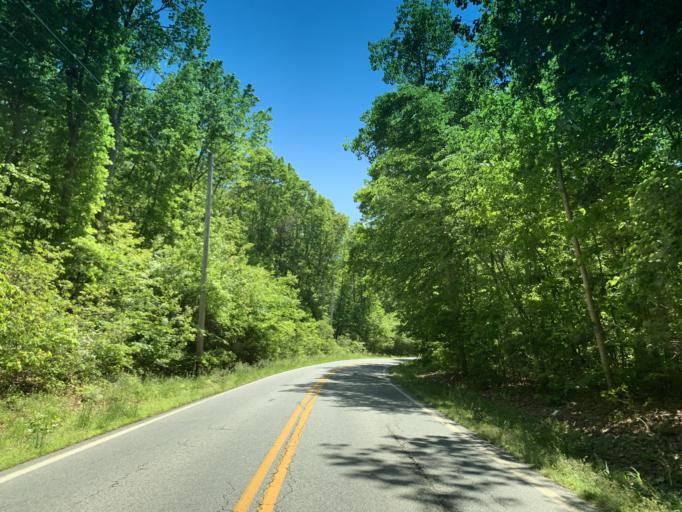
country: US
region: Maryland
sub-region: Cecil County
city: North East
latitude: 39.5647
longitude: -75.8870
